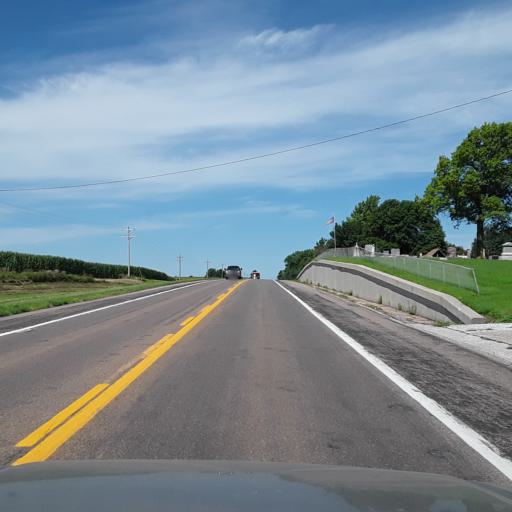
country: US
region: Nebraska
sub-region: Seward County
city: Seward
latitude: 40.9016
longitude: -97.1434
